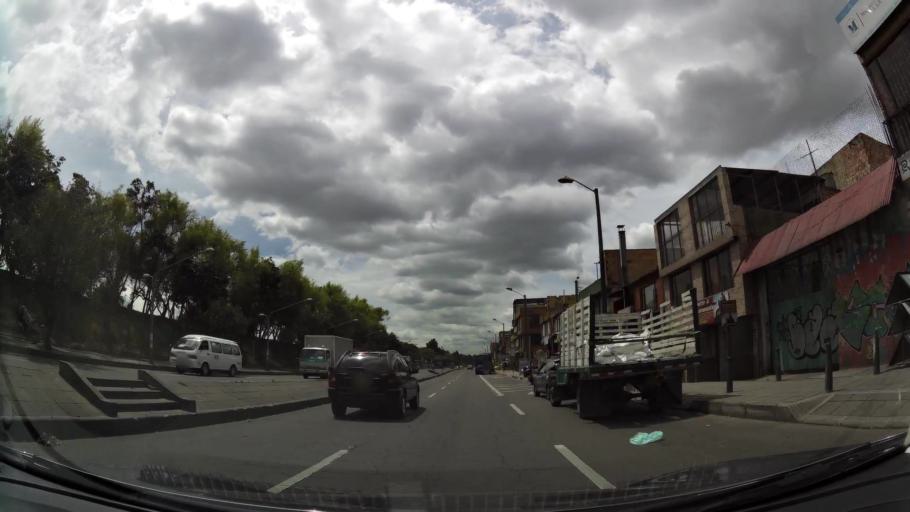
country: CO
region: Cundinamarca
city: Funza
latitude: 4.7008
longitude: -74.1323
